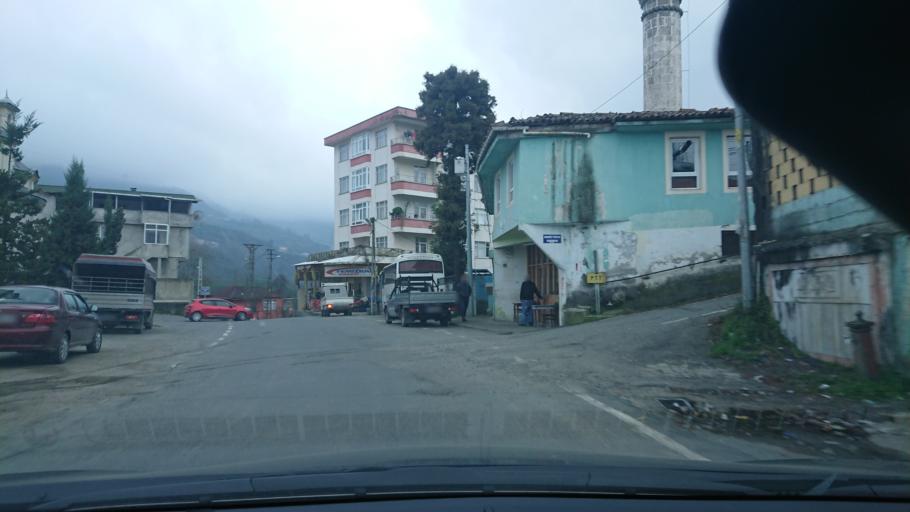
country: TR
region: Rize
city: Rize
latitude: 40.9992
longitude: 40.4874
